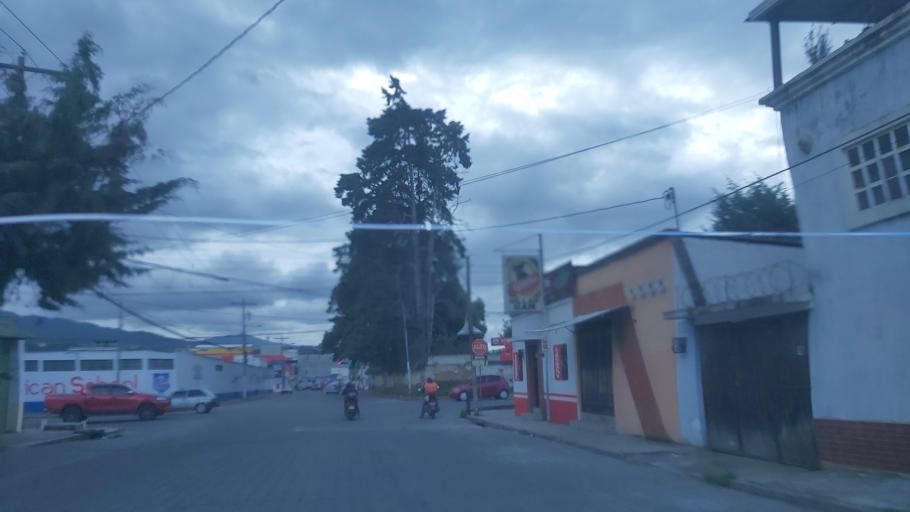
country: GT
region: Quetzaltenango
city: Quetzaltenango
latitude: 14.8498
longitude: -91.5270
